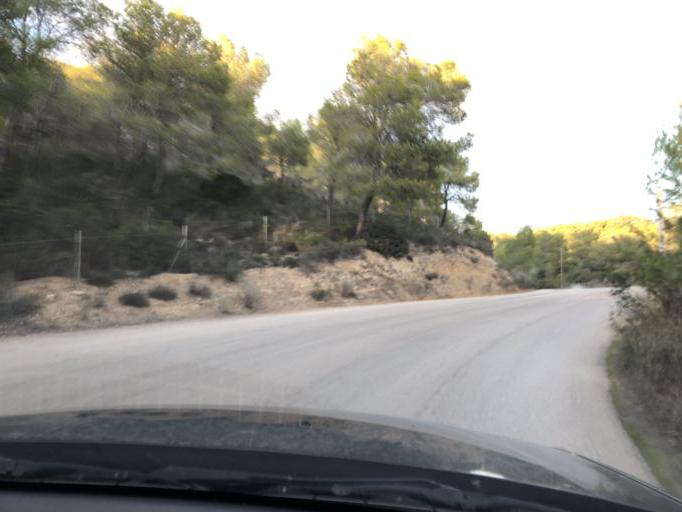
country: ES
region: Balearic Islands
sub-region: Illes Balears
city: Santa Ponsa
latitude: 39.5348
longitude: 2.4804
